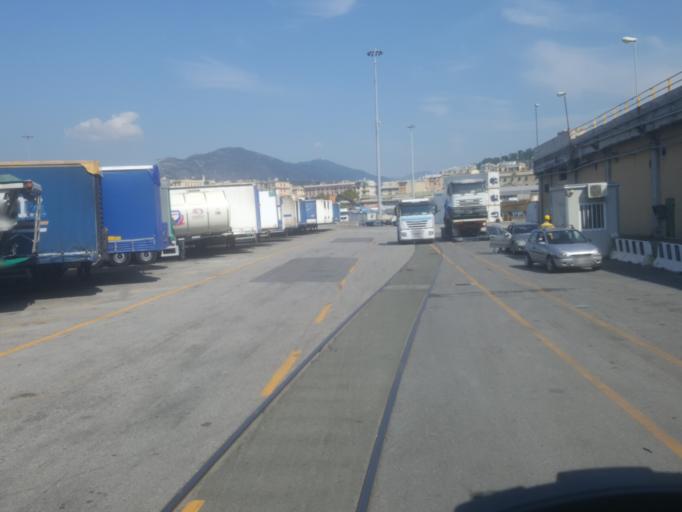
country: IT
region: Liguria
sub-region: Provincia di Genova
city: San Teodoro
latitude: 44.4059
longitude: 8.8900
